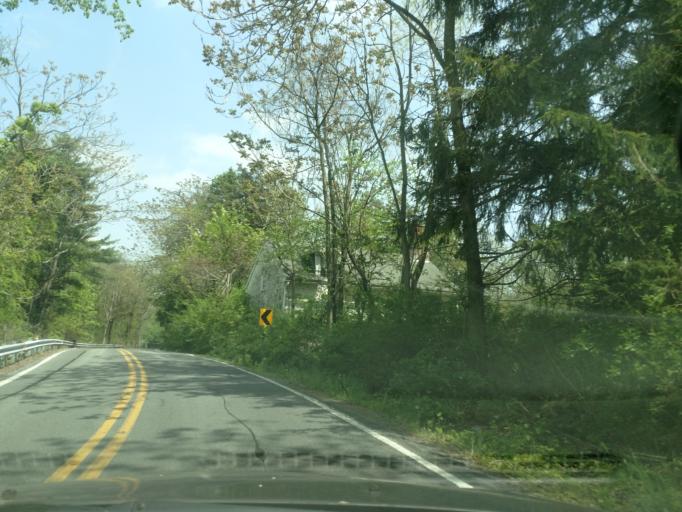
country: US
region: Pennsylvania
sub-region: Chester County
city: Elverson
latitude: 40.1712
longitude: -75.8494
